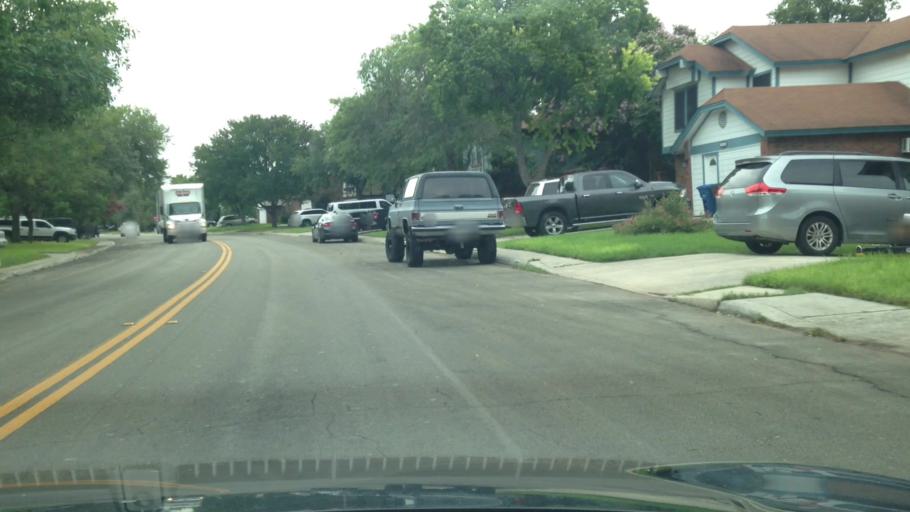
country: US
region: Texas
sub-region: Bexar County
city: Hollywood Park
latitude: 29.5740
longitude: -98.4292
